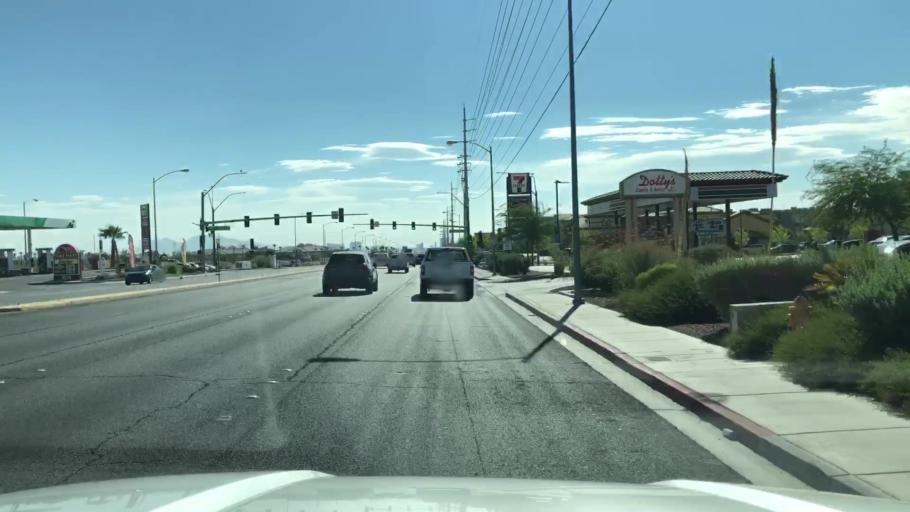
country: US
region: Nevada
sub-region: Clark County
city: Summerlin South
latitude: 36.1149
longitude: -115.2892
